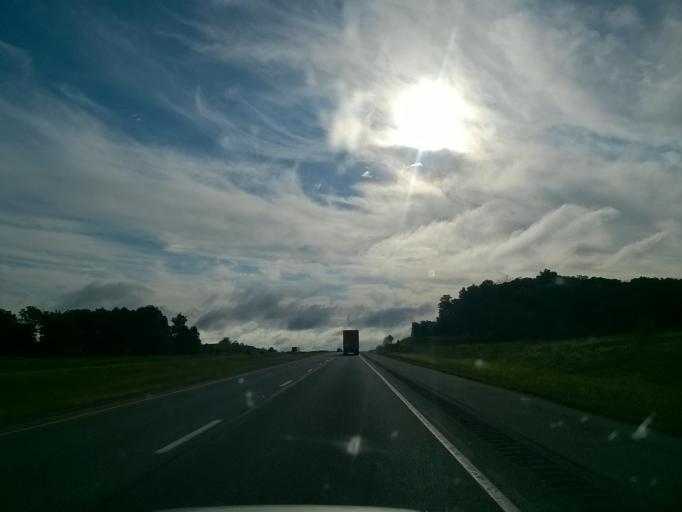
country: US
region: Indiana
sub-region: Dubois County
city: Ferdinand
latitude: 38.2054
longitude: -86.8605
